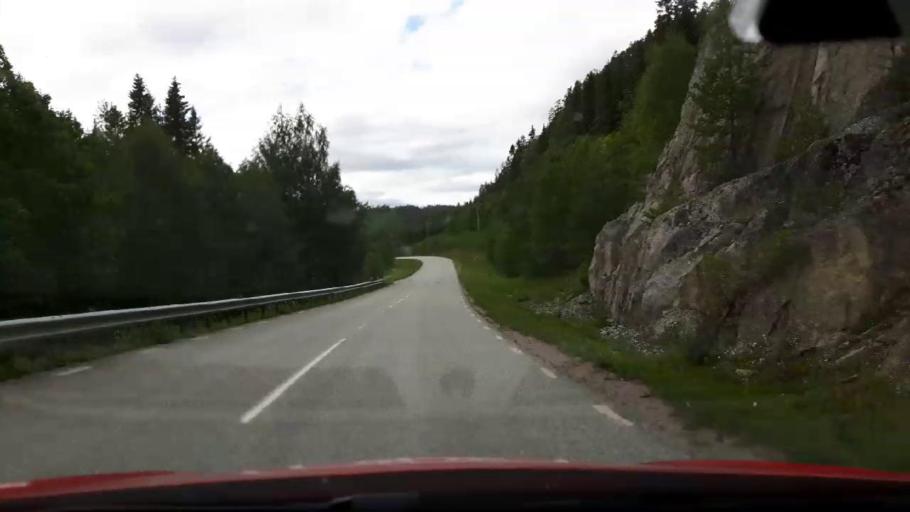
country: SE
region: Jaemtland
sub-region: Ragunda Kommun
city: Hammarstrand
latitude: 62.9649
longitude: 15.9968
